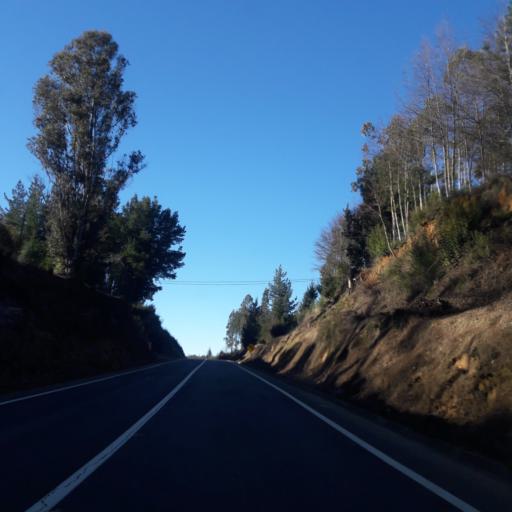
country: CL
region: Biobio
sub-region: Provincia de Biobio
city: La Laja
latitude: -37.3311
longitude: -72.9096
